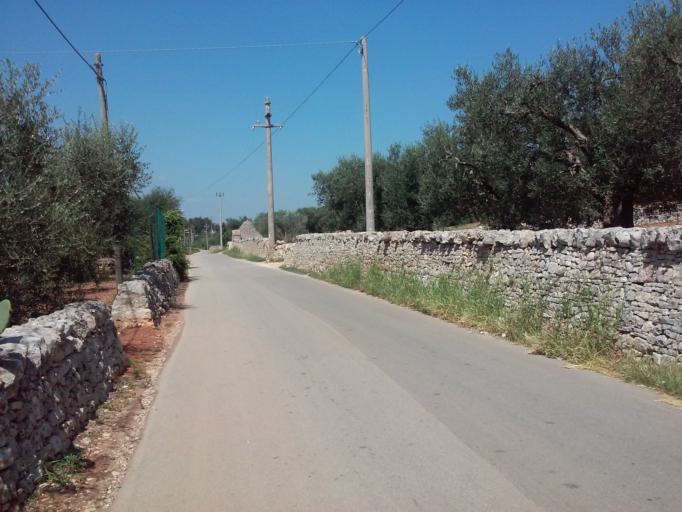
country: IT
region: Apulia
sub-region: Provincia di Bari
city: Alberobello
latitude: 40.7905
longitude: 17.2251
